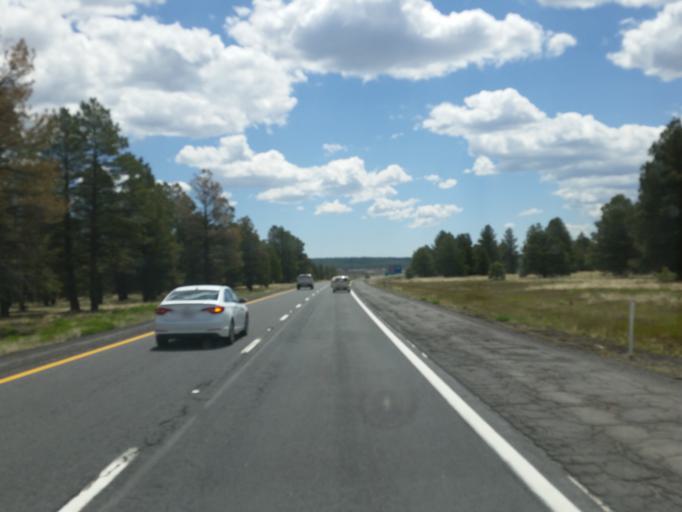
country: US
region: Arizona
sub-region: Coconino County
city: Parks
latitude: 35.2457
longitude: -111.8452
